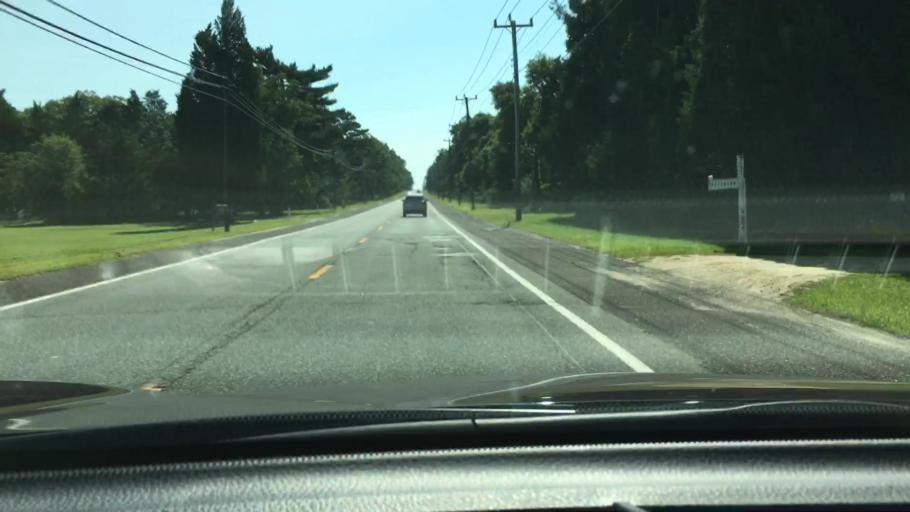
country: US
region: New Jersey
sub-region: Cumberland County
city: Millville
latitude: 39.3837
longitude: -74.9801
